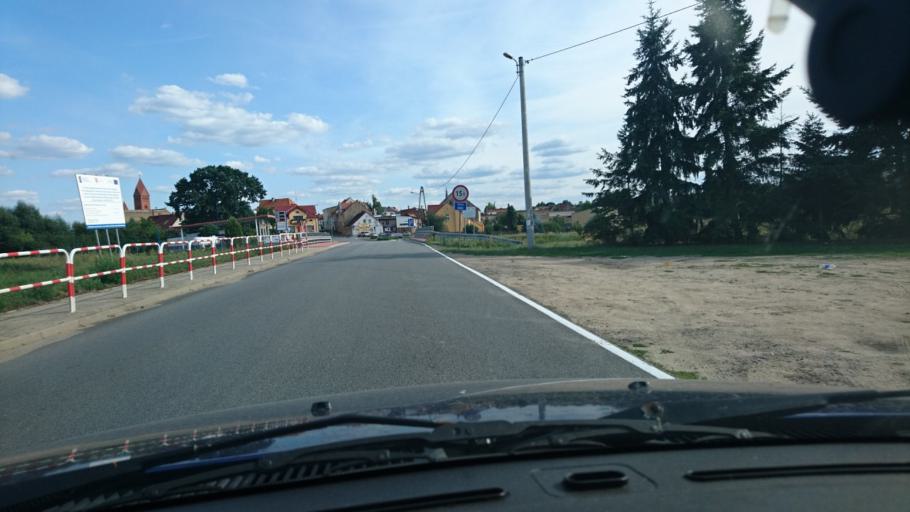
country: PL
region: Greater Poland Voivodeship
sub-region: Powiat rawicki
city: Jutrosin
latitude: 51.6561
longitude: 17.1667
